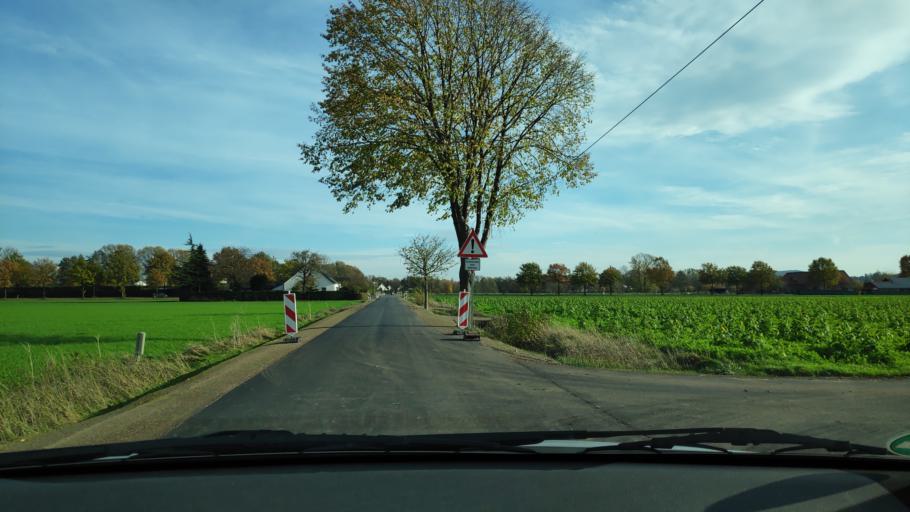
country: DE
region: North Rhine-Westphalia
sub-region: Regierungsbezirk Detmold
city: Minden
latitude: 52.2831
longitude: 8.8614
